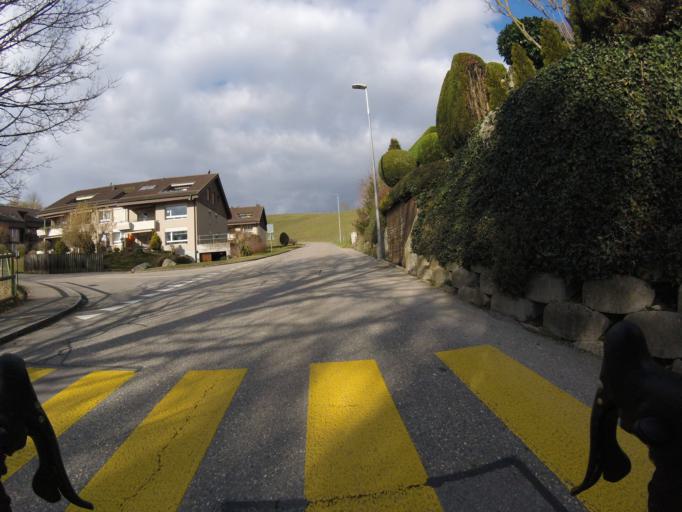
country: CH
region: Bern
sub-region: Bern-Mittelland District
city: Kirchlindach
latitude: 46.9765
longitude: 7.4231
